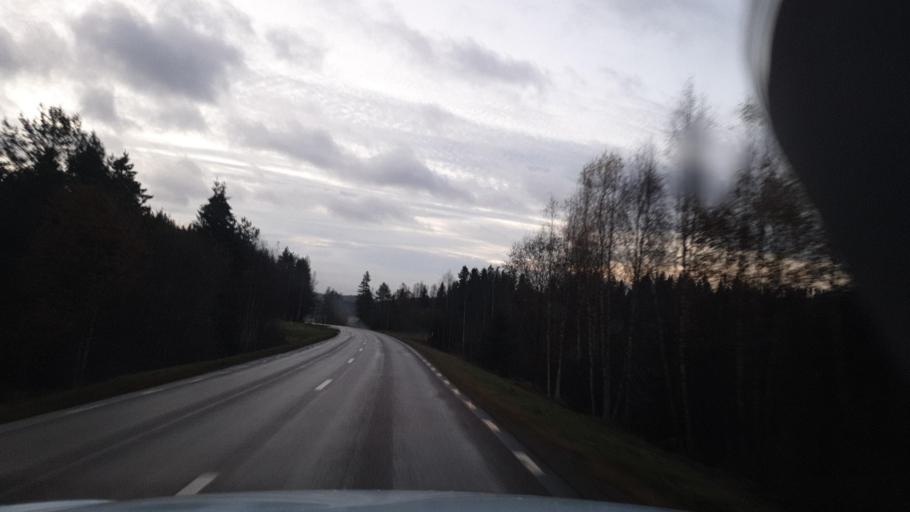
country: SE
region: Vaermland
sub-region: Arvika Kommun
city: Arvika
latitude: 59.6417
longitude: 12.7841
